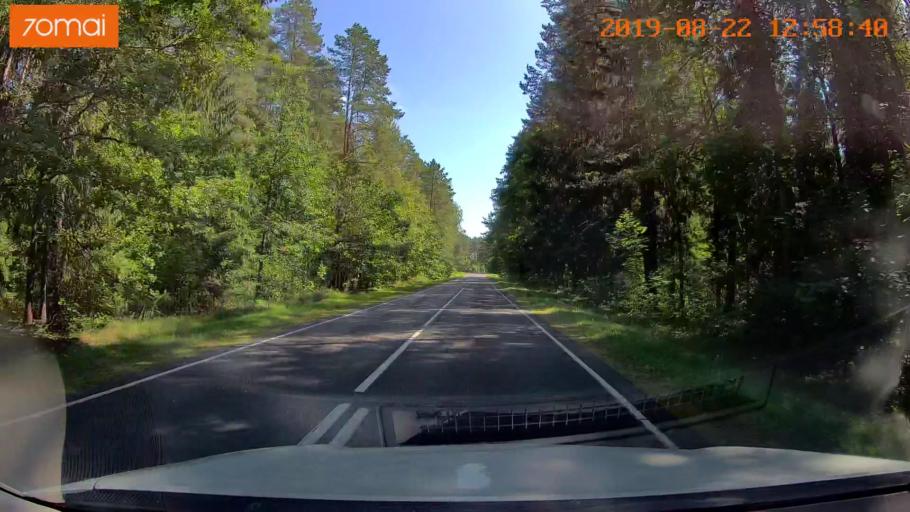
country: BY
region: Minsk
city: Prawdzinski
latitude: 53.4228
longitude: 27.7760
